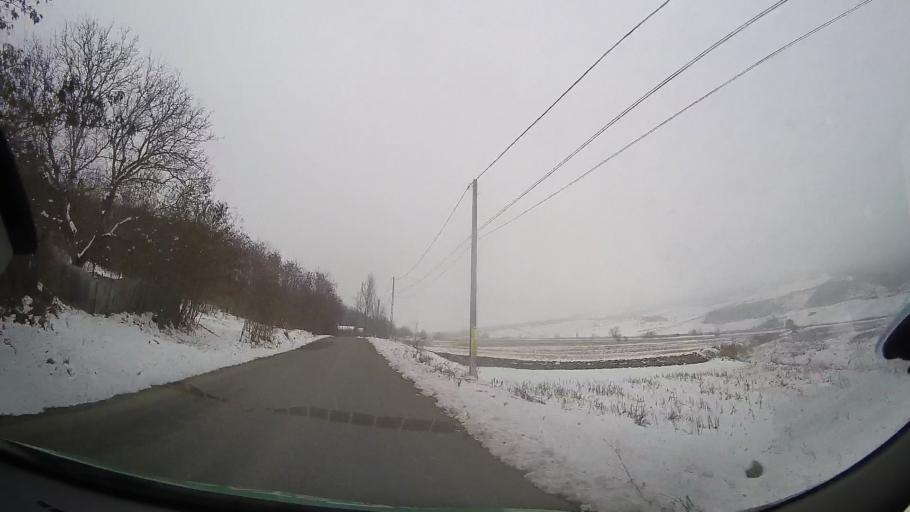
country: RO
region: Bacau
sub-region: Comuna Vultureni
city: Vultureni
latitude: 46.3437
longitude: 27.2907
